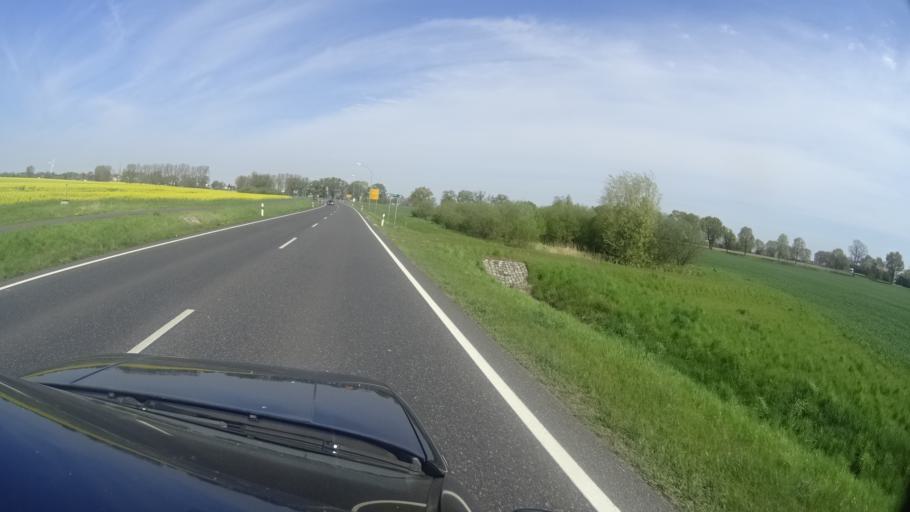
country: DE
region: Brandenburg
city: Nauen
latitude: 52.6099
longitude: 12.8431
